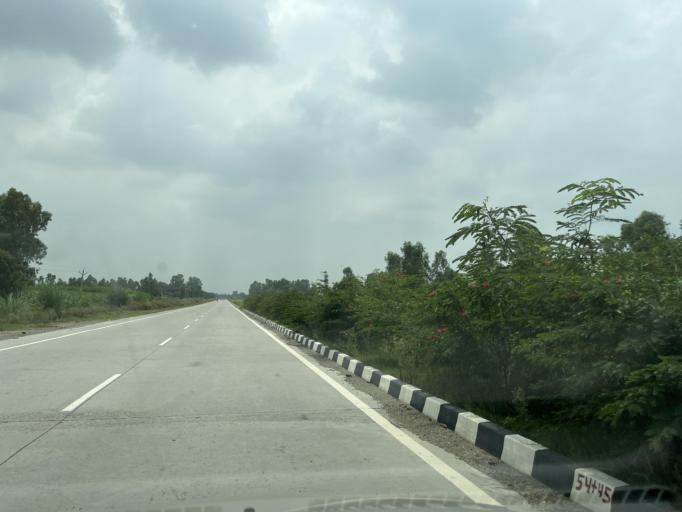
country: IN
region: Uttar Pradesh
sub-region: Bijnor
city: Najibabad
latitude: 29.5594
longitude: 78.3390
